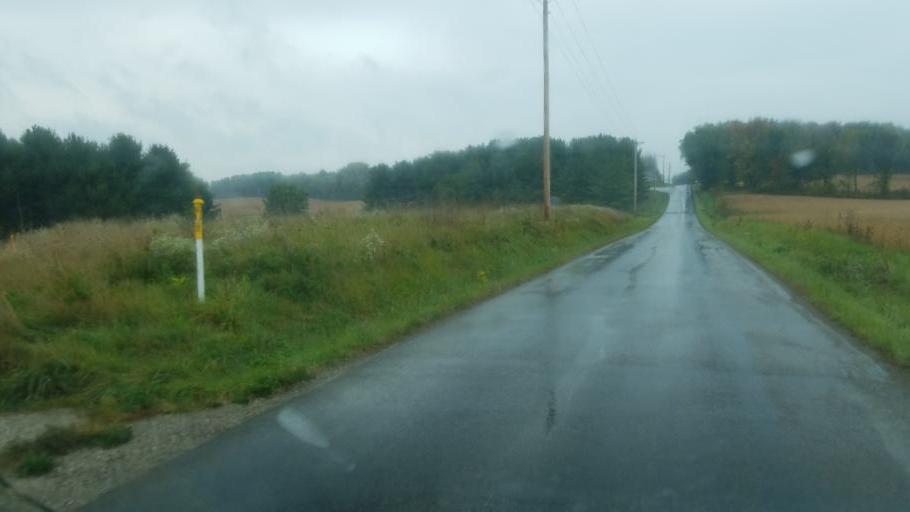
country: US
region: Ohio
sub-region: Ashland County
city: Ashland
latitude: 40.8015
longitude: -82.3574
